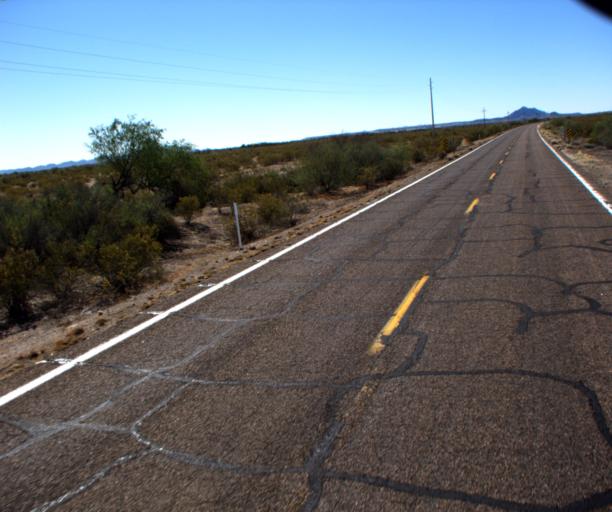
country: US
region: Arizona
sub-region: Pima County
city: Ajo
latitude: 32.4588
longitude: -112.8727
